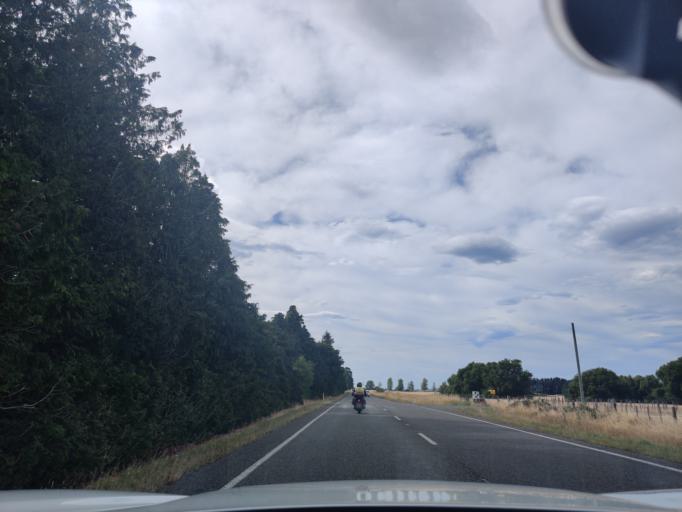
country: NZ
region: Wellington
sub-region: Masterton District
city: Masterton
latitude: -40.8706
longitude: 175.6484
